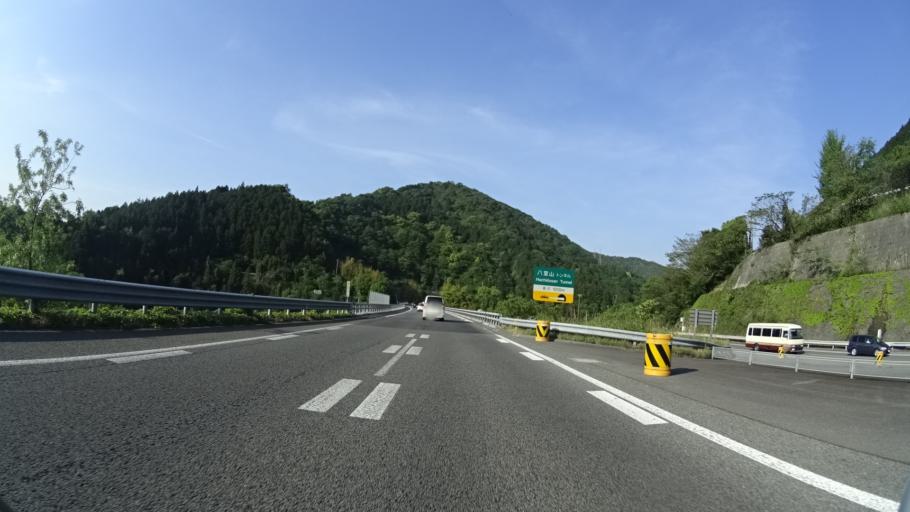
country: JP
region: Ehime
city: Saijo
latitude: 33.8890
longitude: 133.1956
